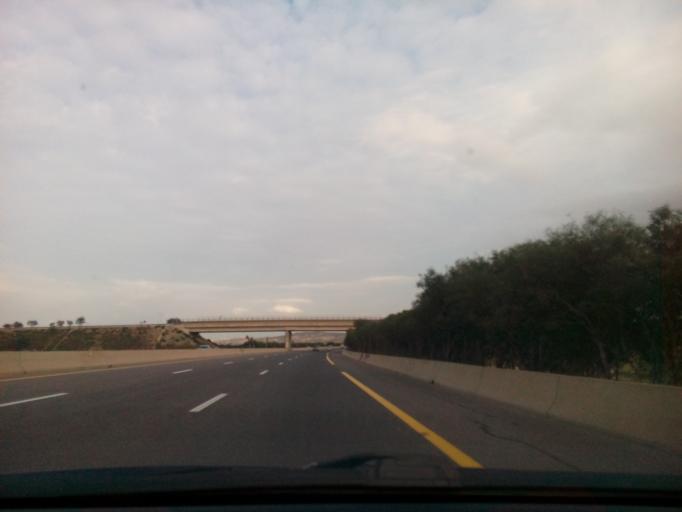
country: DZ
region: Mostaganem
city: Mostaganem
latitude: 35.7037
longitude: 0.1940
